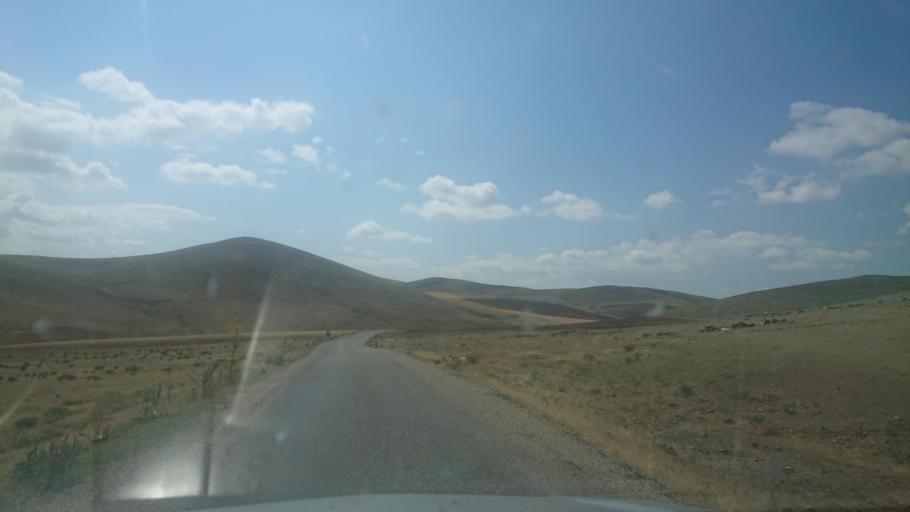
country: TR
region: Aksaray
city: Sariyahsi
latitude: 39.0112
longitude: 33.9470
